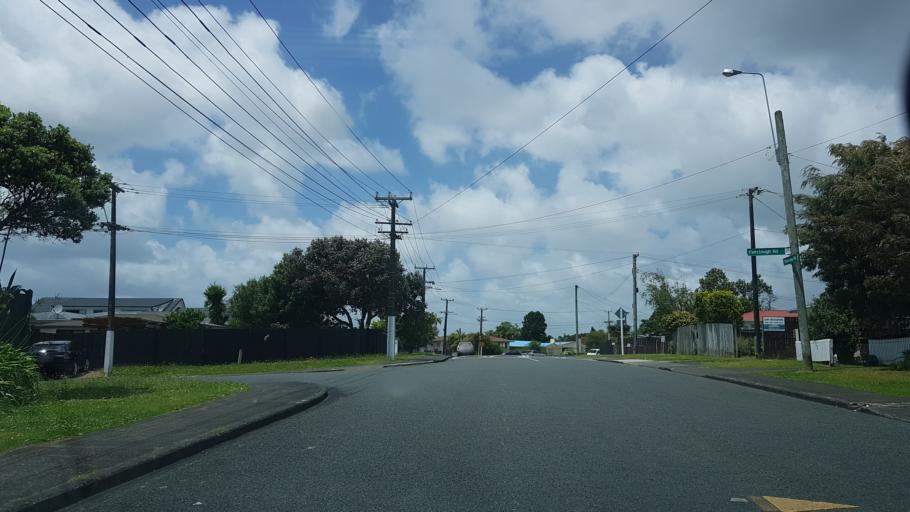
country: NZ
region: Auckland
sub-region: Auckland
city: North Shore
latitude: -36.7945
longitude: 174.6917
